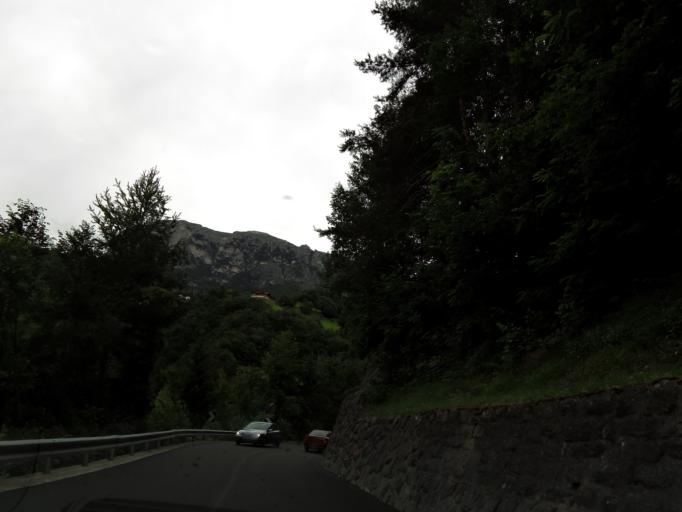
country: IT
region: Trentino-Alto Adige
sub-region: Bolzano
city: Fie Allo Sciliar
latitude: 46.5083
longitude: 11.5071
